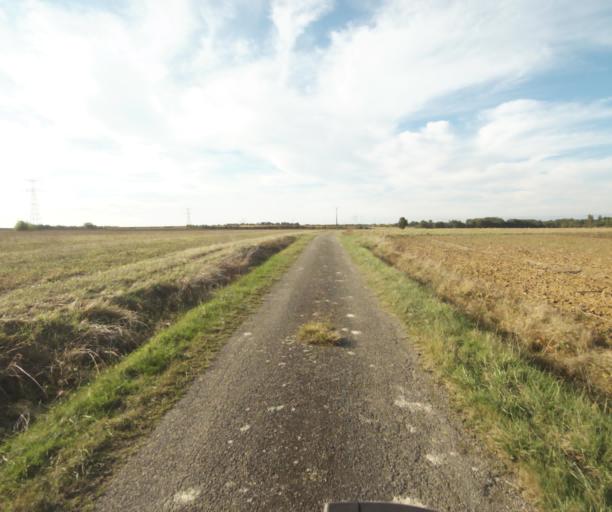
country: FR
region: Midi-Pyrenees
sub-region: Departement du Tarn-et-Garonne
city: Finhan
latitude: 43.9069
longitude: 1.1132
